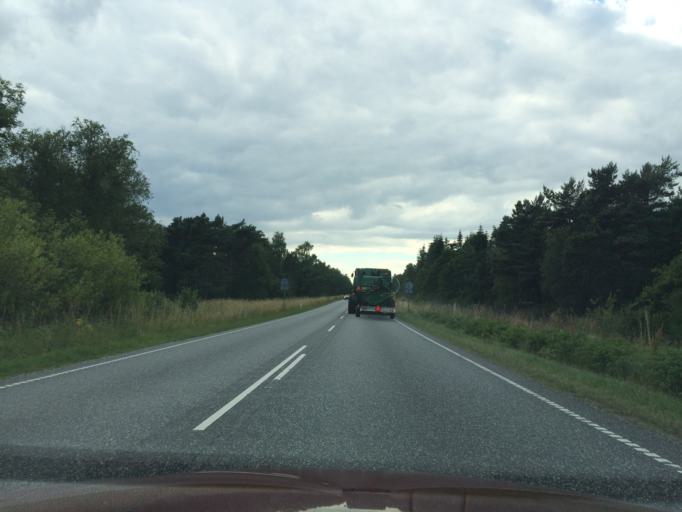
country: DK
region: Central Jutland
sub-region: Syddjurs Kommune
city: Ebeltoft
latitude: 56.2929
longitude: 10.6096
